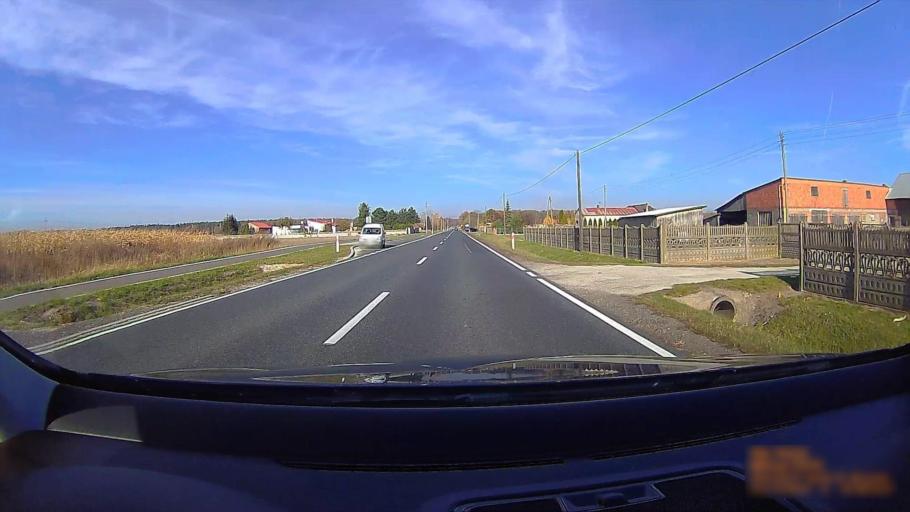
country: PL
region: Greater Poland Voivodeship
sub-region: Powiat kaliski
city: Stawiszyn
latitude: 51.9616
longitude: 18.1376
